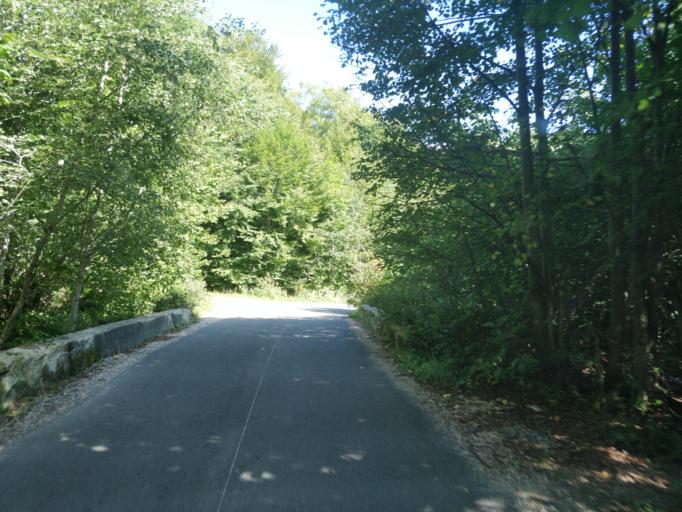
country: RO
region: Cluj
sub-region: Comuna Sacueu
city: Sacuieu
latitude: 46.7879
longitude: 22.8878
